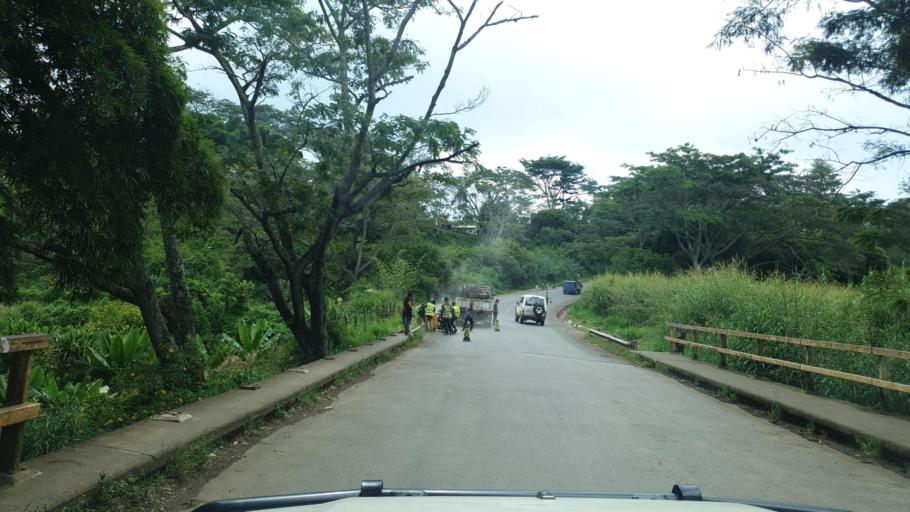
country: PG
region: Eastern Highlands
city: Goroka
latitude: -6.0442
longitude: 145.3743
